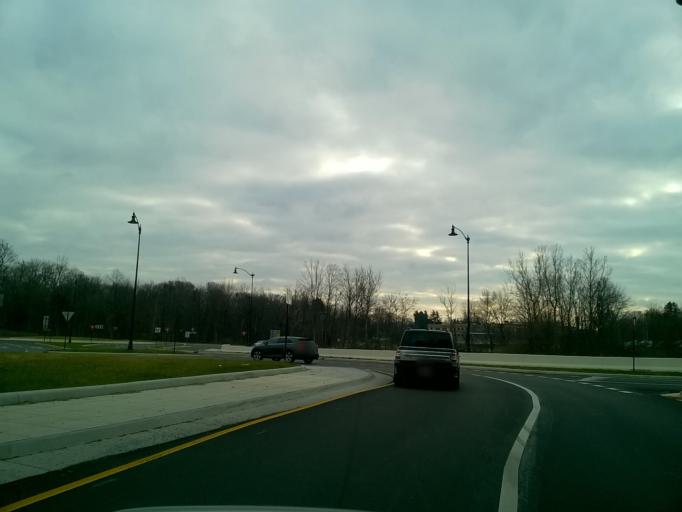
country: US
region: Indiana
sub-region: Hamilton County
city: Carmel
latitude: 39.9842
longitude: -86.1417
